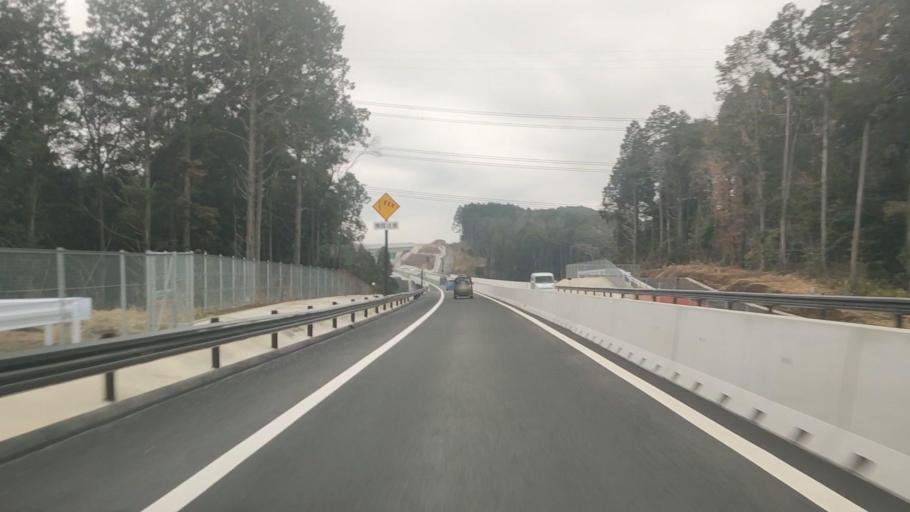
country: JP
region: Kumamoto
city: Ozu
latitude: 32.8991
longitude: 130.9046
